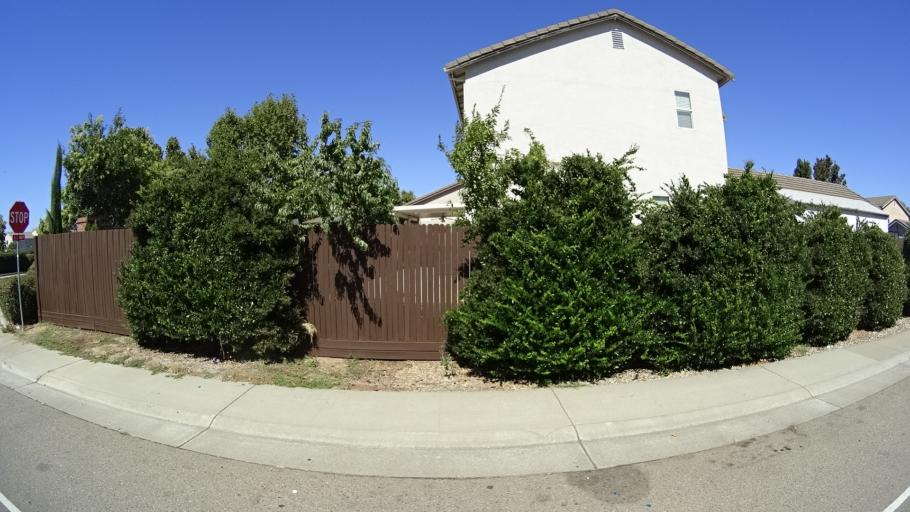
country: US
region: California
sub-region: Sacramento County
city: Elk Grove
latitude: 38.4188
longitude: -121.3433
